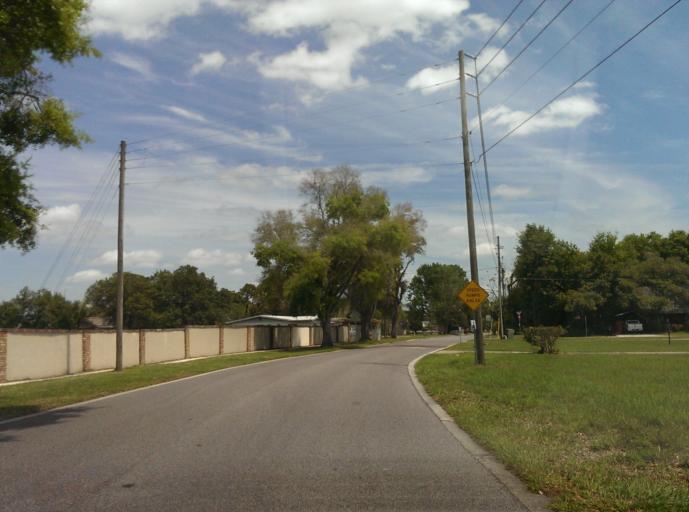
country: US
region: Florida
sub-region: Orange County
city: Doctor Phillips
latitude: 28.4827
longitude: -81.4843
